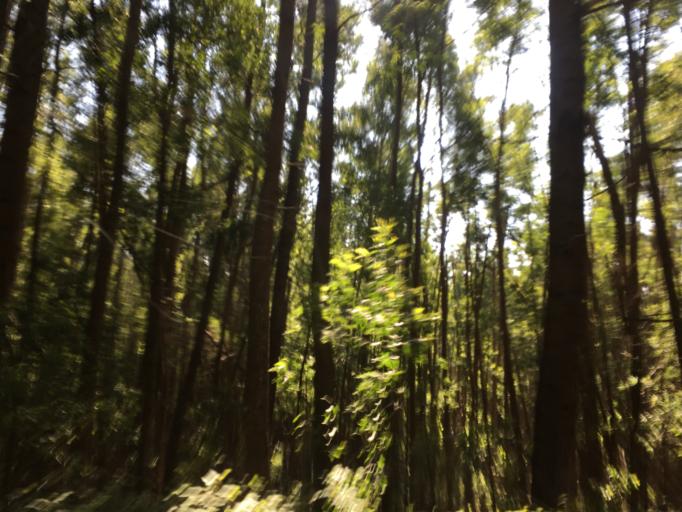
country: PT
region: Lisbon
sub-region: Sintra
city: Colares
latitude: 38.7774
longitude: -9.4376
